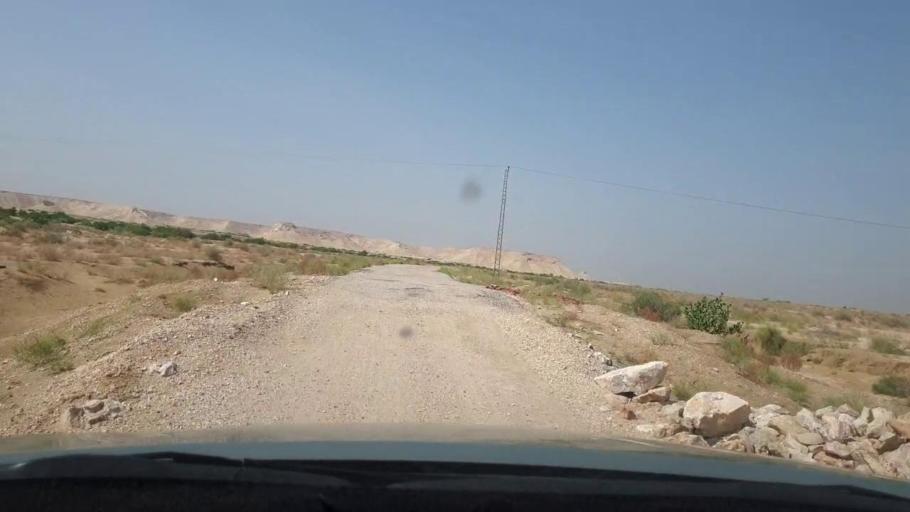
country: PK
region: Sindh
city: Kot Diji
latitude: 27.3296
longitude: 68.8156
